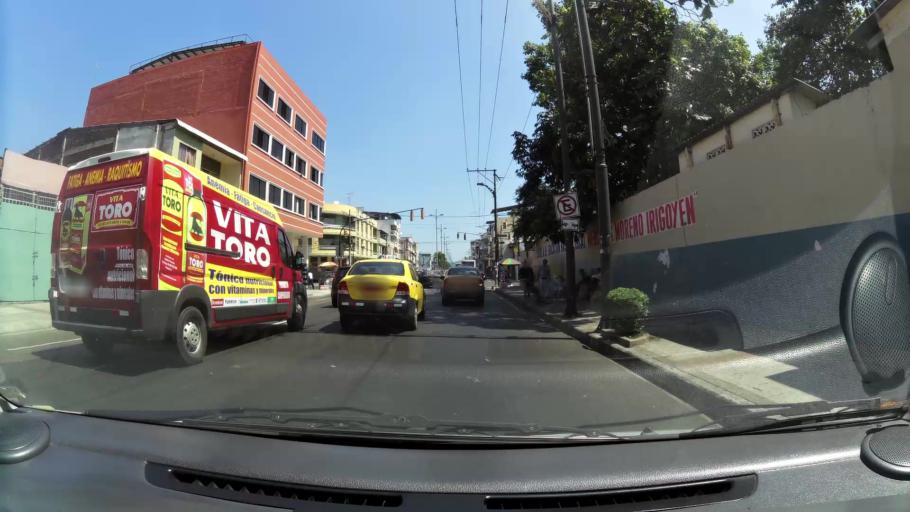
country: EC
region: Guayas
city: Guayaquil
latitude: -2.2031
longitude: -79.9106
